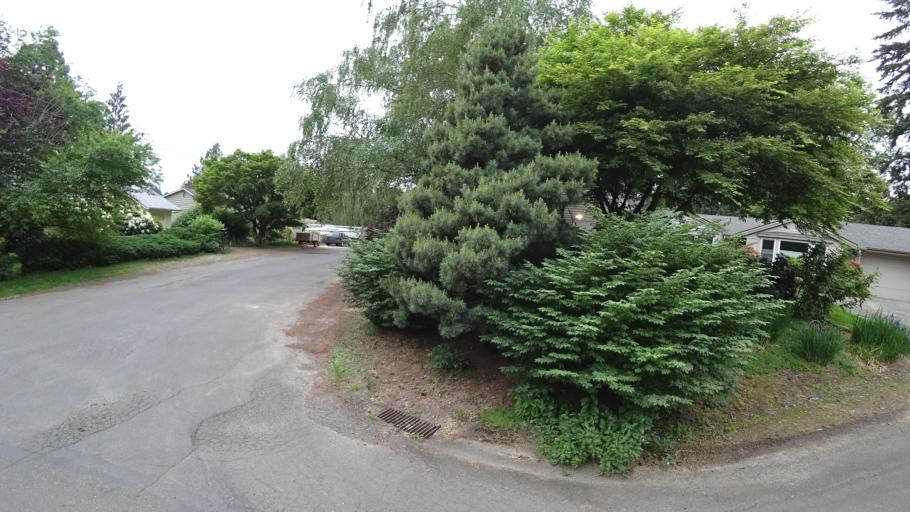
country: US
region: Oregon
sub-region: Multnomah County
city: Portland
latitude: 45.4855
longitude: -122.7032
